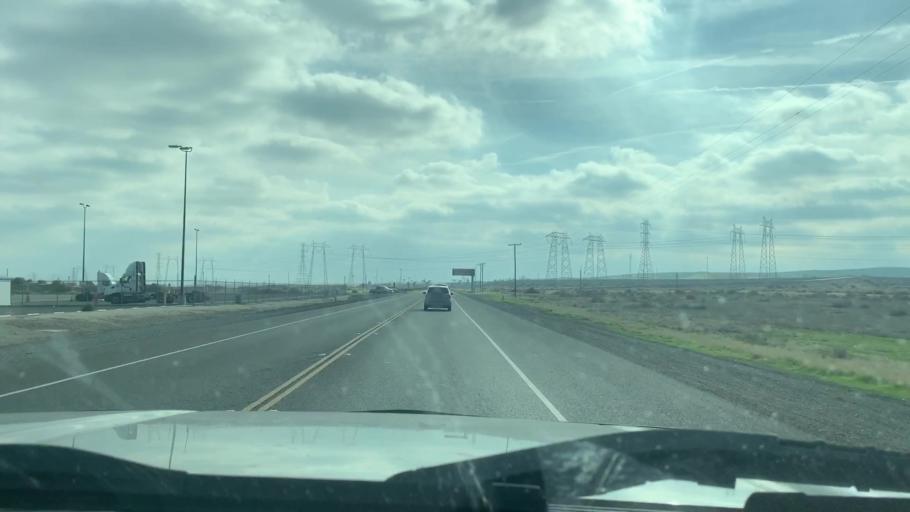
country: US
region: California
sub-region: Kings County
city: Kettleman City
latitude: 36.0044
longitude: -119.9594
